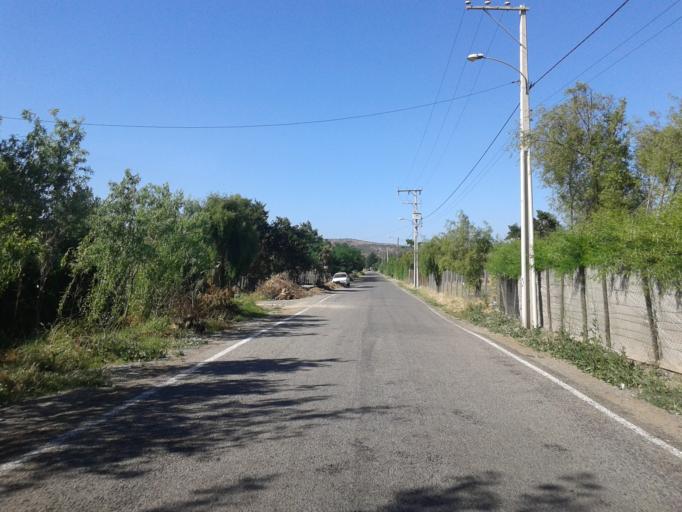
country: CL
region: Valparaiso
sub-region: Provincia de Marga Marga
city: Limache
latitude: -32.9768
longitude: -71.2947
